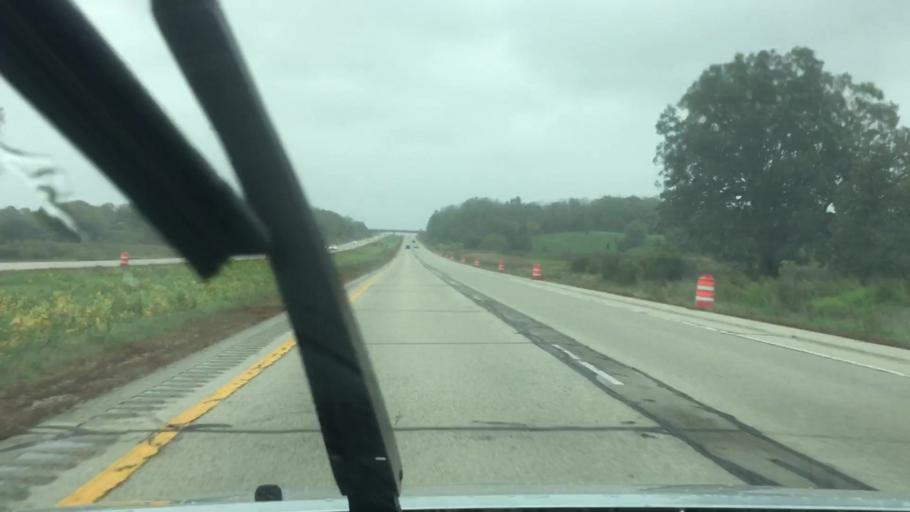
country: US
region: Wisconsin
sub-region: Walworth County
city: Lake Geneva
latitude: 42.5788
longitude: -88.3878
